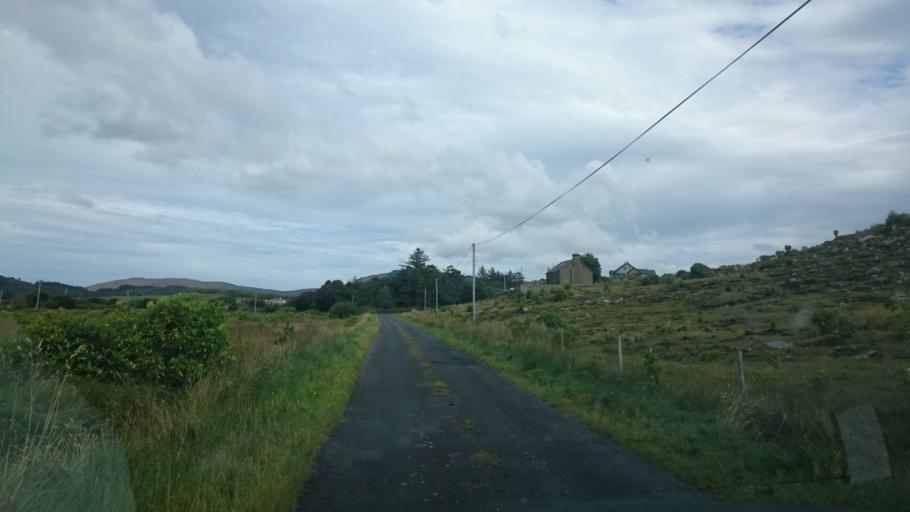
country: IE
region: Connaught
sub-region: Maigh Eo
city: Westport
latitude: 53.9707
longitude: -9.5688
